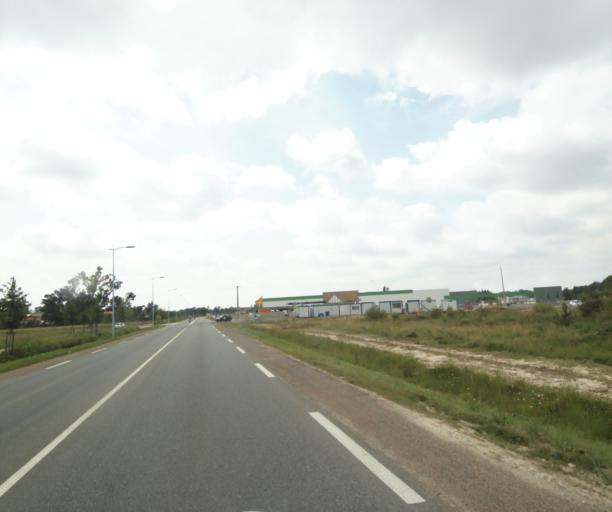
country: FR
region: Midi-Pyrenees
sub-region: Departement du Tarn-et-Garonne
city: Montauban
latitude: 44.0442
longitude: 1.3864
